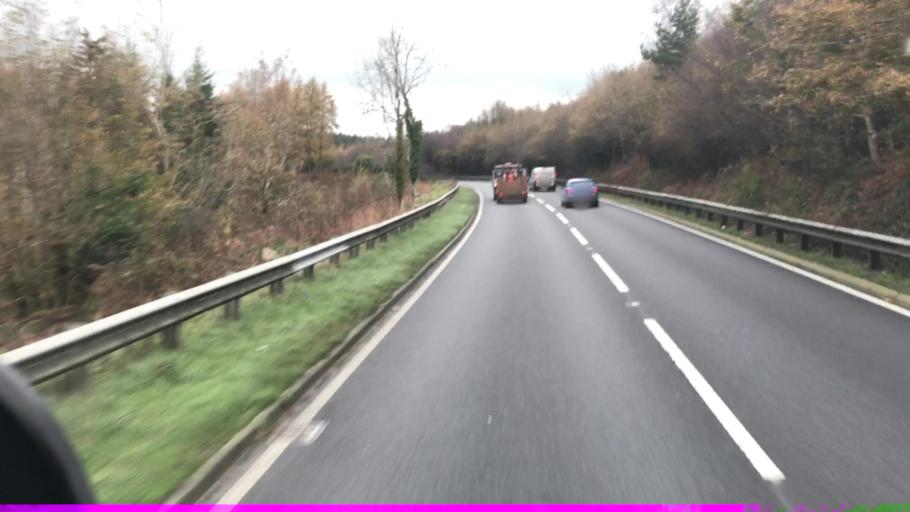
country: GB
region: England
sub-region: Devon
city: Chudleigh
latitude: 50.6327
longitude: -3.5664
